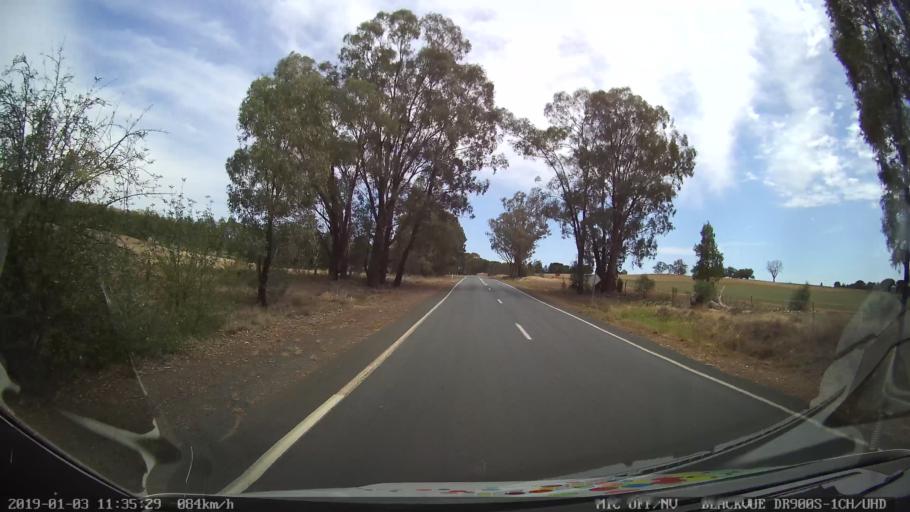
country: AU
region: New South Wales
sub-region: Weddin
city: Grenfell
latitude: -33.9215
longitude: 148.1596
